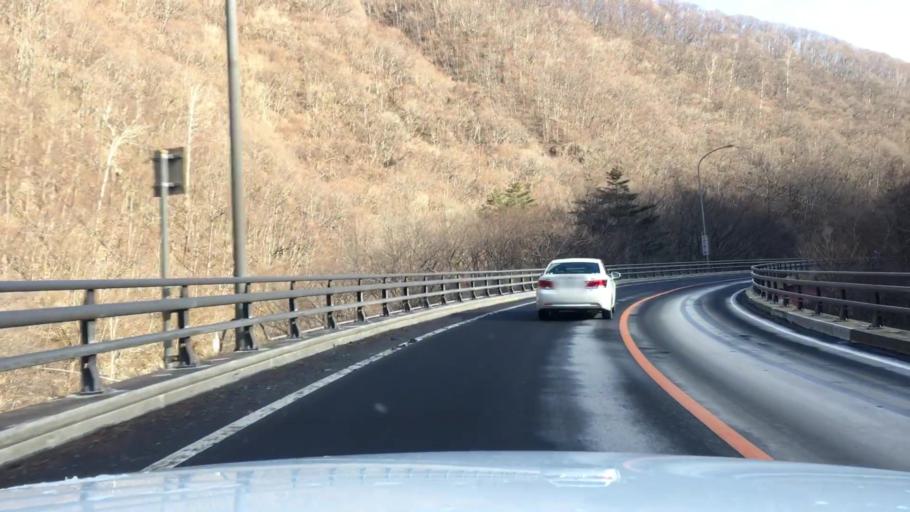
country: JP
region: Iwate
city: Tono
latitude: 39.6212
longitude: 141.5045
